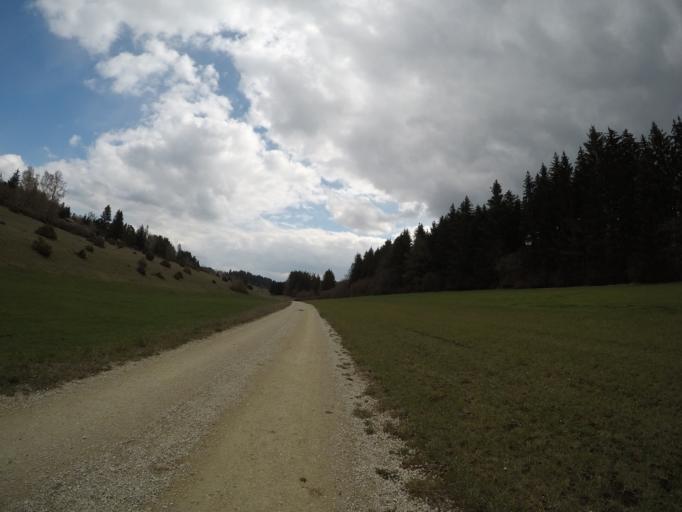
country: DE
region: Baden-Wuerttemberg
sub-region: Tuebingen Region
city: Merklingen
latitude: 48.5077
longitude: 9.7786
